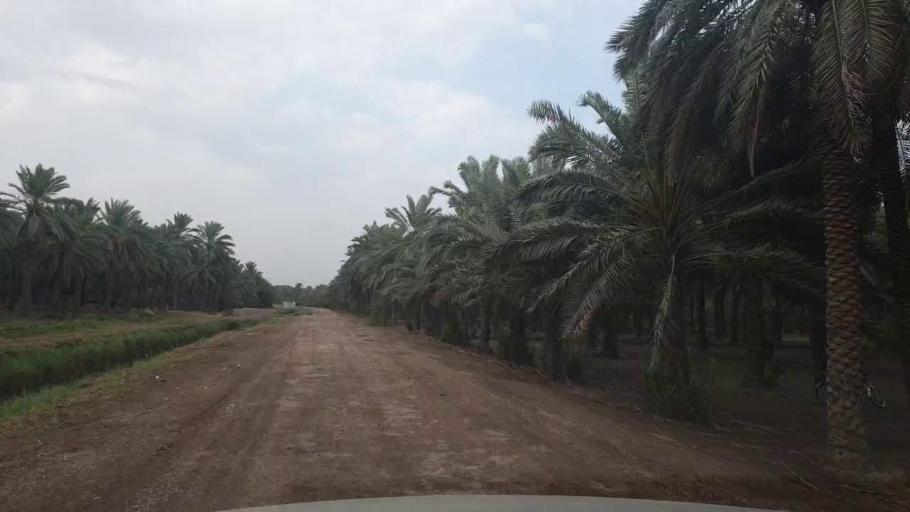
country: PK
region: Sindh
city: Sukkur
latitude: 27.6152
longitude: 68.8367
